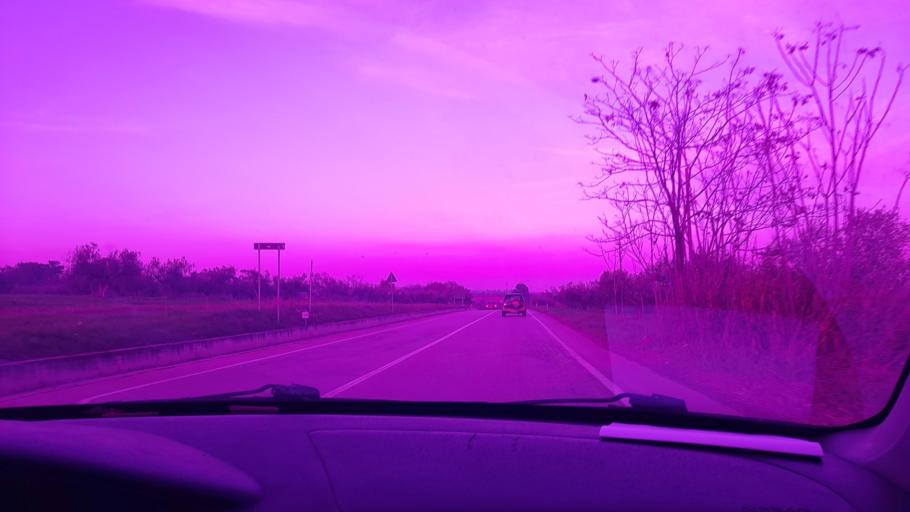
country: IT
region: Abruzzo
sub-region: Provincia di Pescara
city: Cappelle sul Tavo
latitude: 42.4883
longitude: 14.0802
